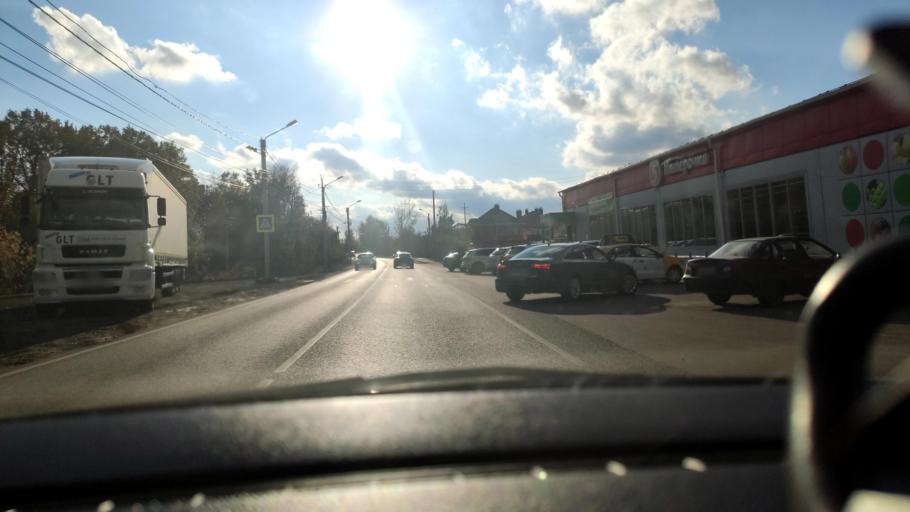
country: RU
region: Voronezj
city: Pridonskoy
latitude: 51.6450
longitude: 39.0971
